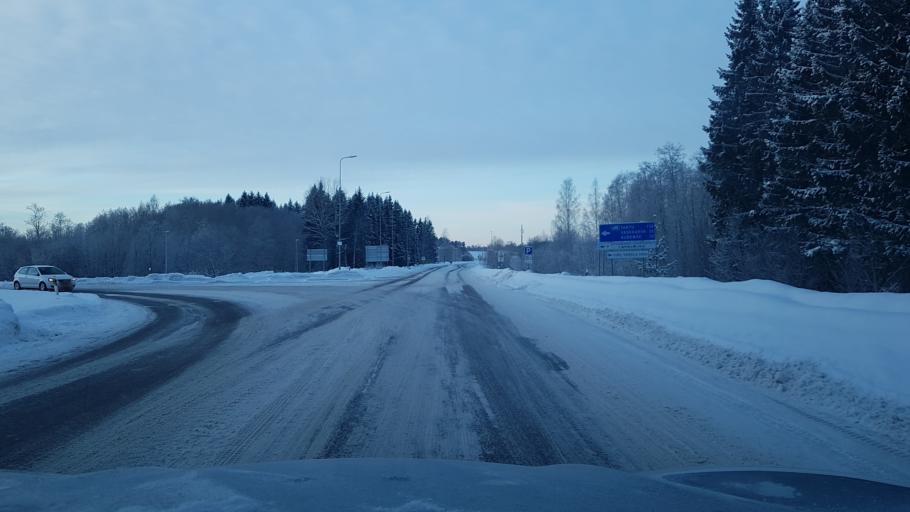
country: EE
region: Ida-Virumaa
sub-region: Johvi vald
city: Johvi
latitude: 59.3622
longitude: 27.4618
